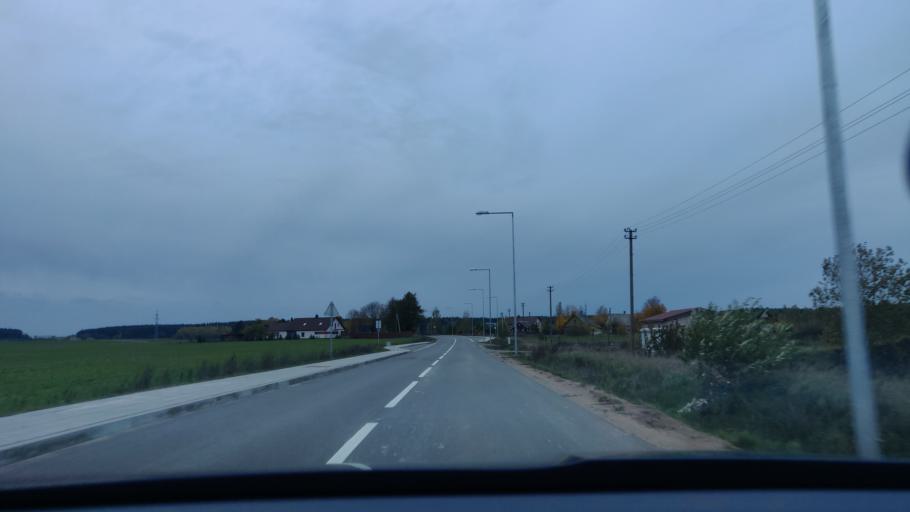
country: LT
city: Lentvaris
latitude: 54.5898
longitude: 25.0496
